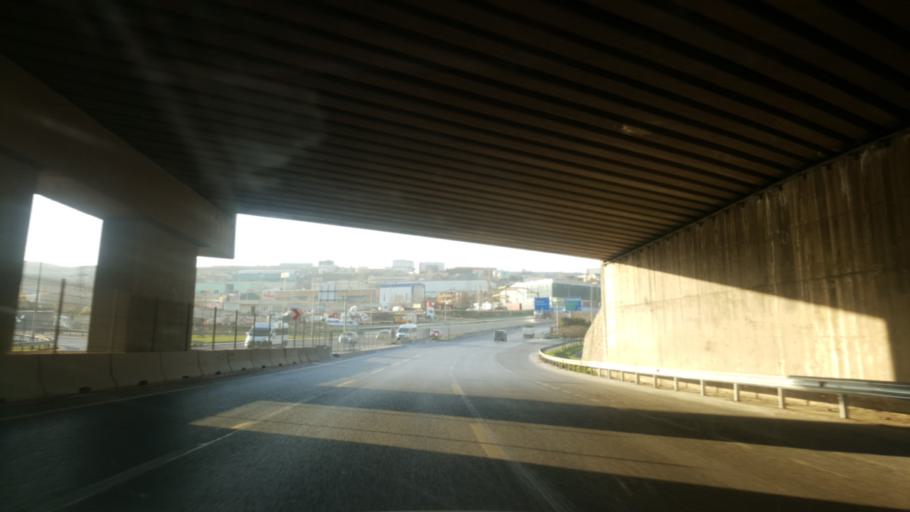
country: TR
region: Kocaeli
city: Tavsanli
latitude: 40.7907
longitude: 29.5285
